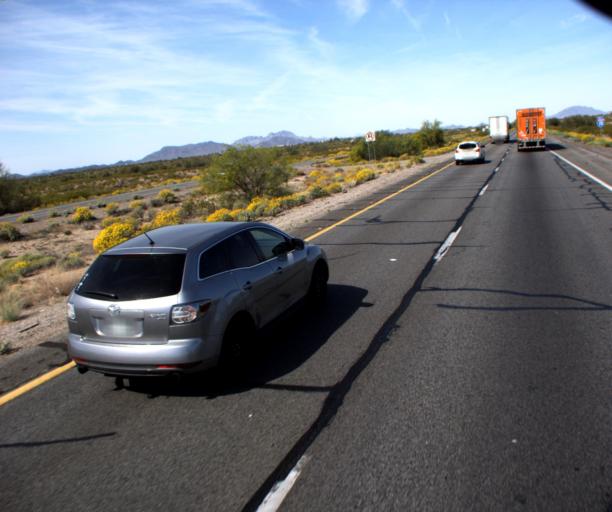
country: US
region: Arizona
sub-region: Maricopa County
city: Buckeye
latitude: 33.4647
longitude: -112.7901
